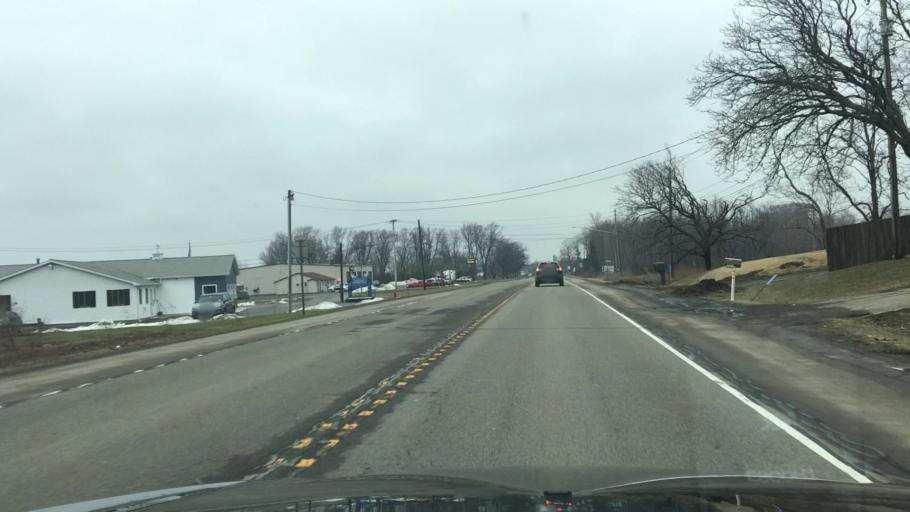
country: US
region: New York
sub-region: Chautauqua County
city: Fredonia
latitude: 42.4377
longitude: -79.3062
